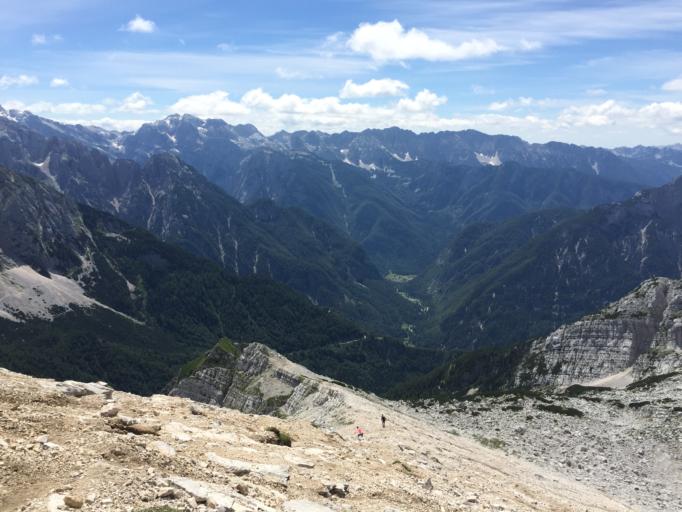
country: SI
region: Kranjska Gora
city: Kranjska Gora
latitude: 46.4364
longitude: 13.7311
